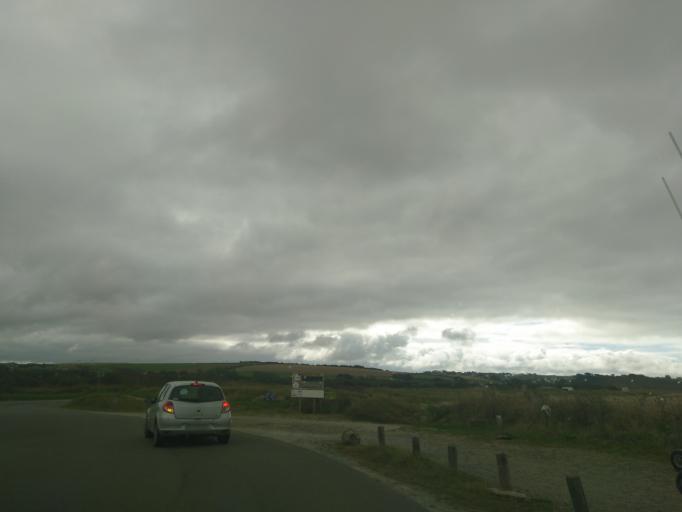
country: FR
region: Brittany
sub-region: Departement du Finistere
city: Plomodiern
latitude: 48.1848
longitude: -4.2958
